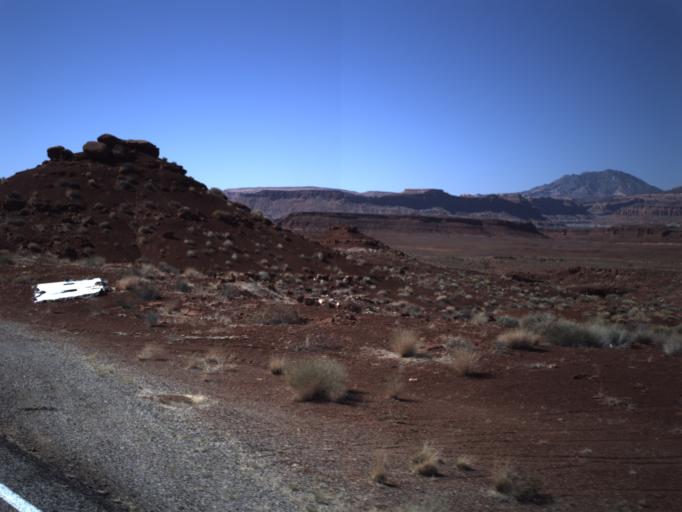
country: US
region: Utah
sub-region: San Juan County
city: Blanding
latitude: 37.8521
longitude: -110.3536
